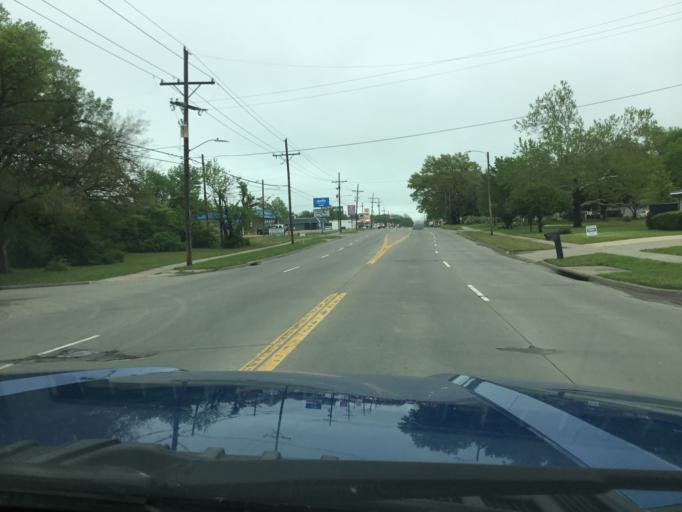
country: US
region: Kansas
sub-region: Shawnee County
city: Topeka
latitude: 39.0294
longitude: -95.7326
